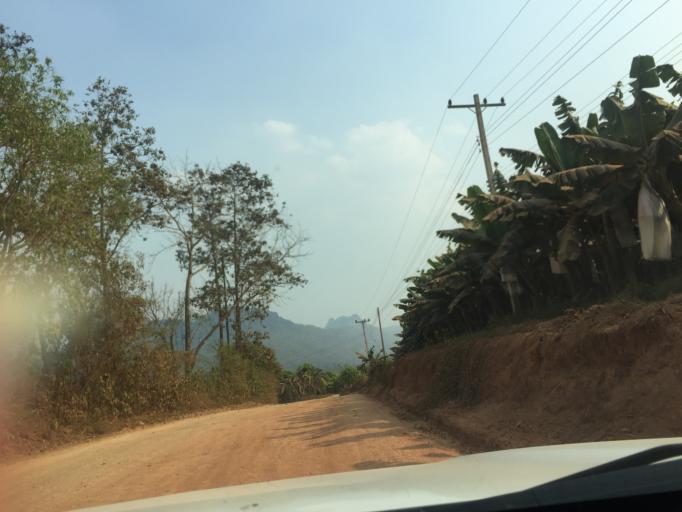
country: LA
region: Xiagnabouli
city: Sainyabuli
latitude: 19.2120
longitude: 101.6937
